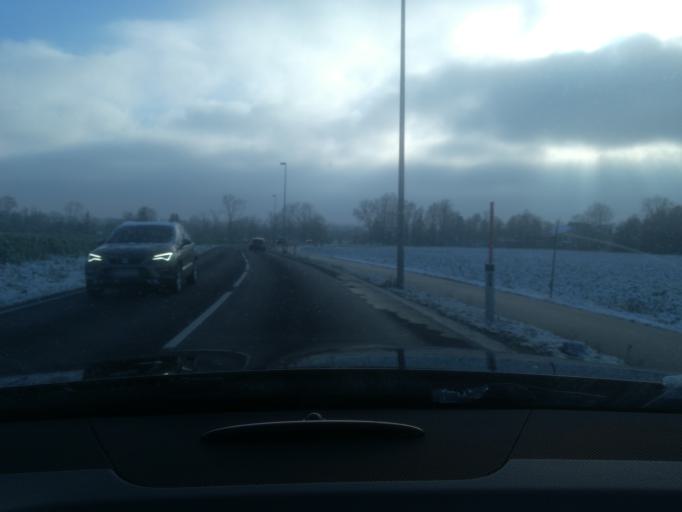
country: AT
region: Upper Austria
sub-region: Wels-Land
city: Marchtrenk
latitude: 48.1861
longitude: 14.1184
